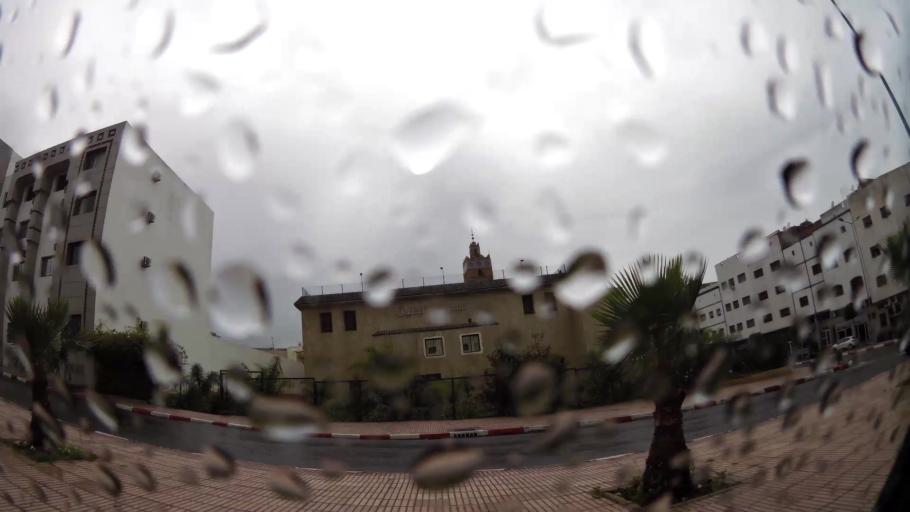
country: MA
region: Grand Casablanca
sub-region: Mediouna
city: Tit Mellil
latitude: 33.6180
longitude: -7.4853
